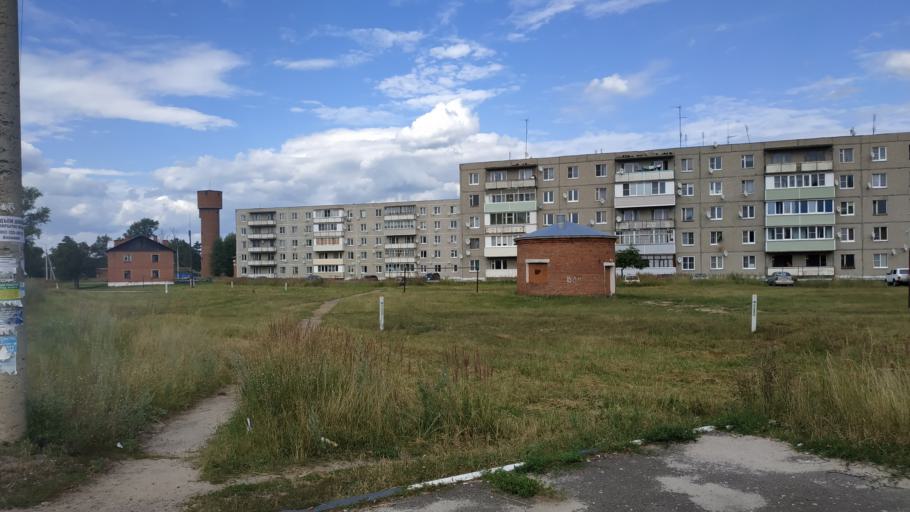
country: RU
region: Moskovskaya
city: Radovitskiy
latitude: 55.1283
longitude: 39.5455
